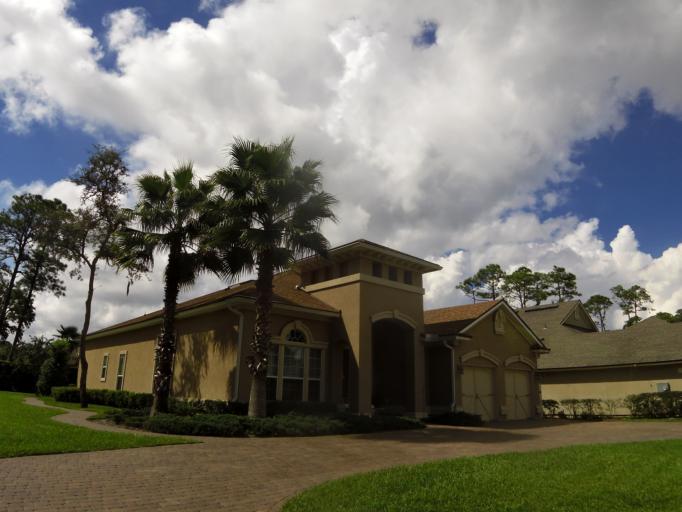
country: US
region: Florida
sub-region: Nassau County
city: Fernandina Beach
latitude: 30.6247
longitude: -81.4624
